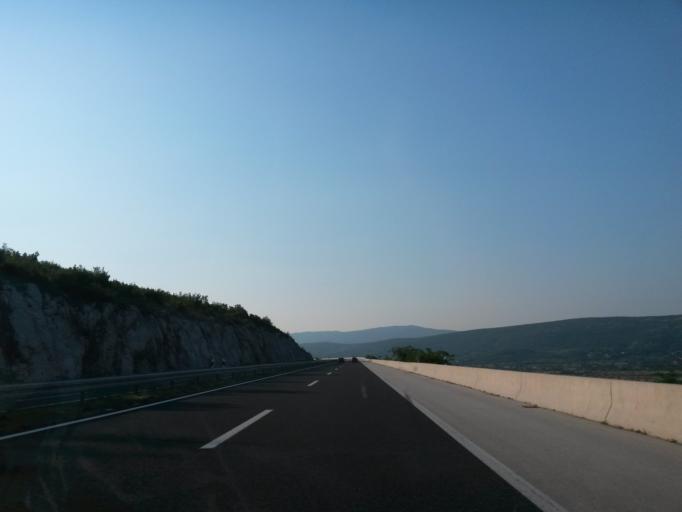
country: HR
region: Splitsko-Dalmatinska
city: Dugopolje
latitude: 43.5945
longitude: 16.6261
